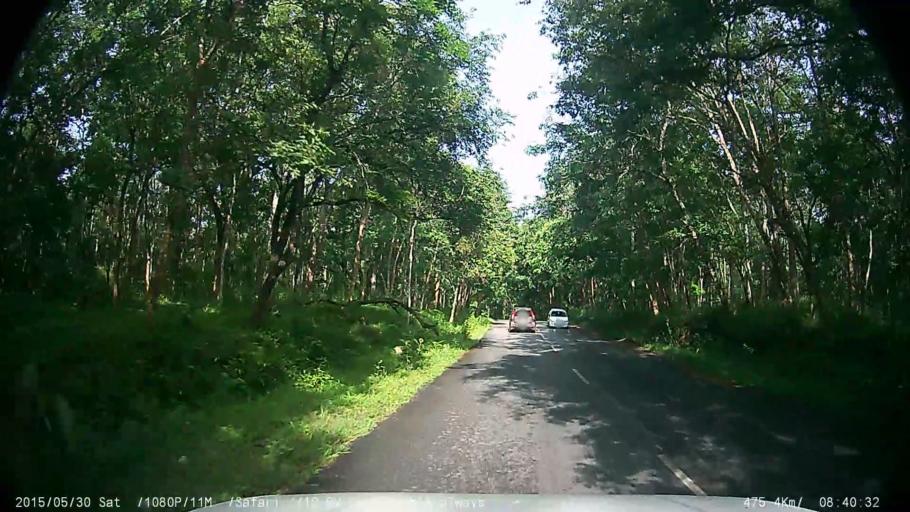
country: IN
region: Tamil Nadu
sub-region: Nilgiri
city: Naduvattam
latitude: 11.7079
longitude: 76.4135
